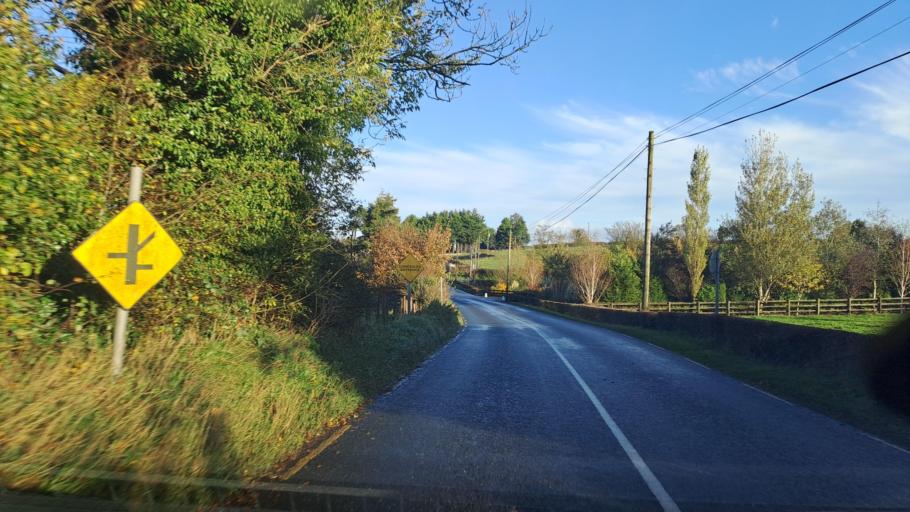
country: IE
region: Ulster
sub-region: County Monaghan
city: Monaghan
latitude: 54.2050
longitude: -6.9864
